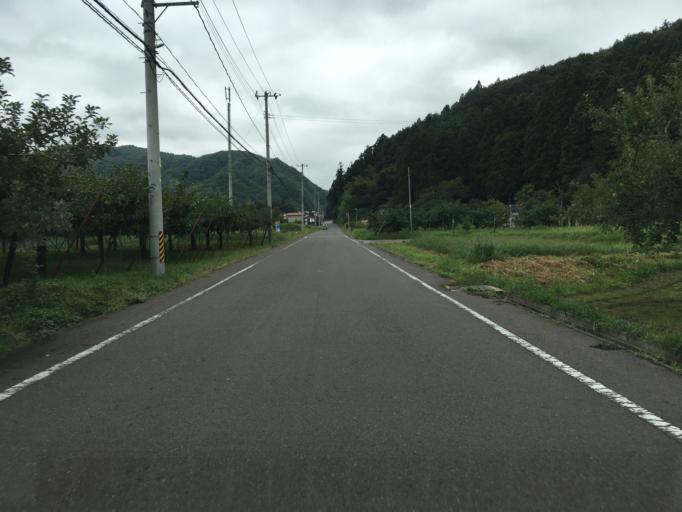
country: JP
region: Fukushima
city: Fukushima-shi
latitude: 37.7948
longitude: 140.3853
